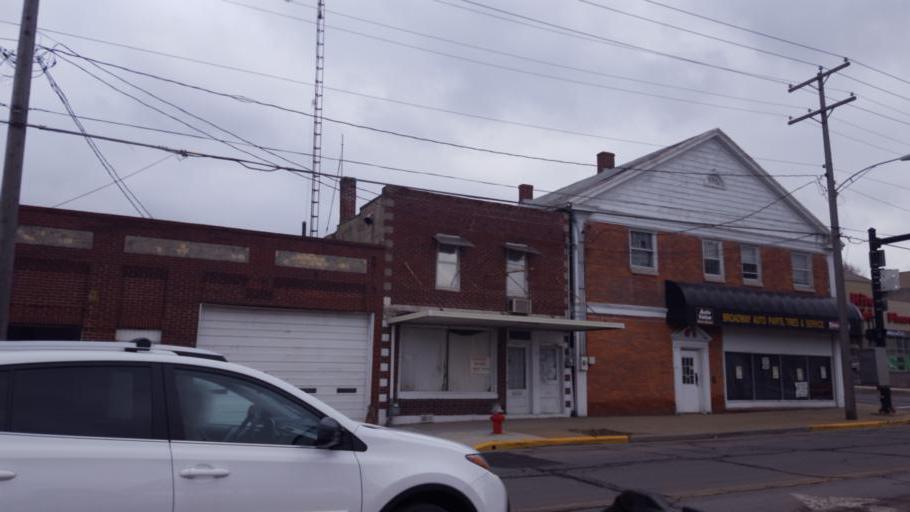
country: US
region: Ohio
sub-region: Richland County
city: Shelby
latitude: 40.8817
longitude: -82.6565
